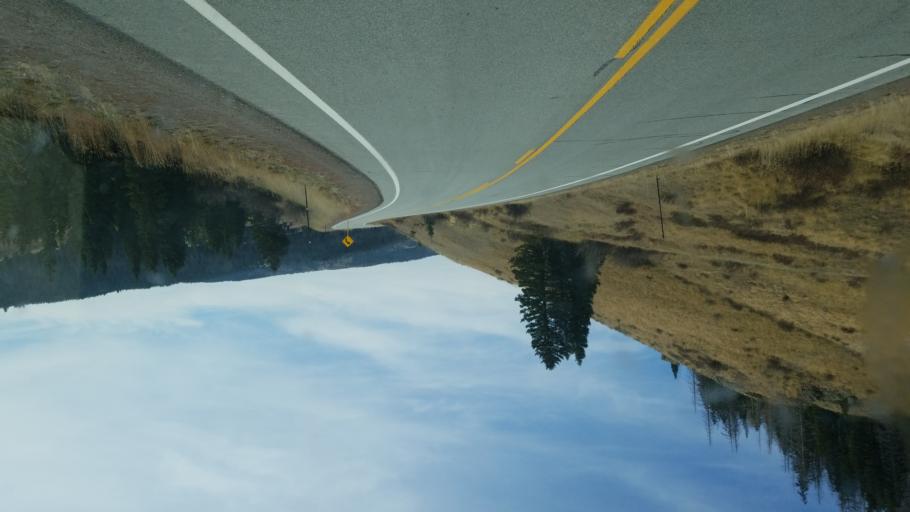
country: US
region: New Mexico
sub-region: Rio Arriba County
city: Chama
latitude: 37.0193
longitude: -106.4395
